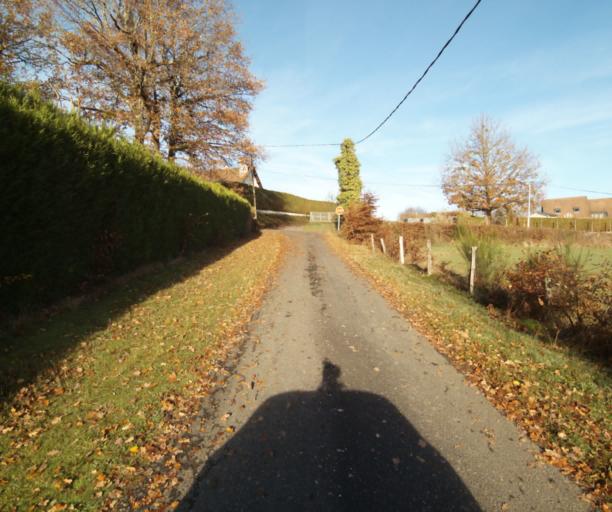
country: FR
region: Limousin
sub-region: Departement de la Correze
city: Laguenne
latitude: 45.2547
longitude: 1.7923
